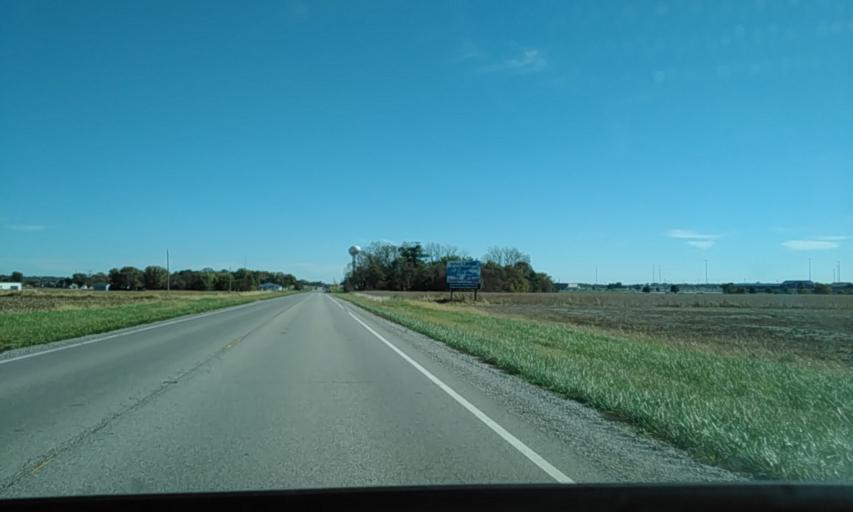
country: US
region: Illinois
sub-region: Bond County
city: Greenville
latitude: 38.8674
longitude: -89.4196
